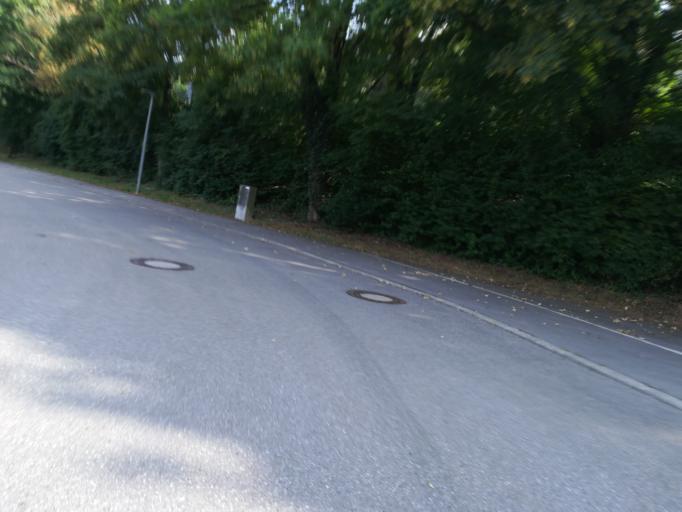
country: DE
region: Baden-Wuerttemberg
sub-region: Freiburg Region
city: Singen
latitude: 47.7557
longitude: 8.8171
